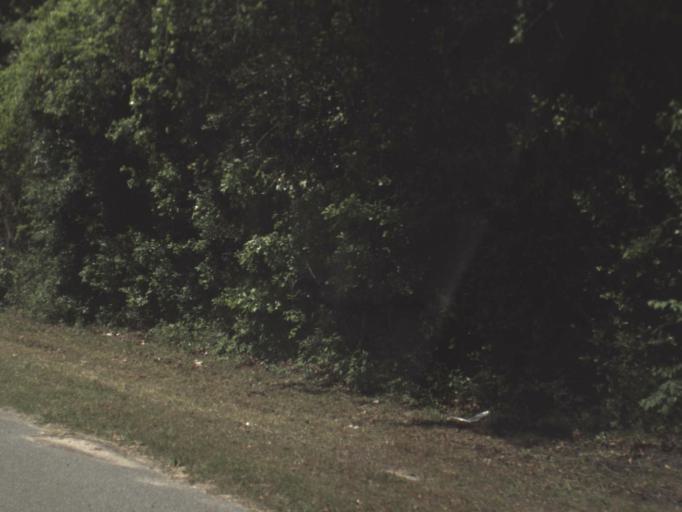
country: US
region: Florida
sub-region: Jefferson County
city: Monticello
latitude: 30.5219
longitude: -84.0244
